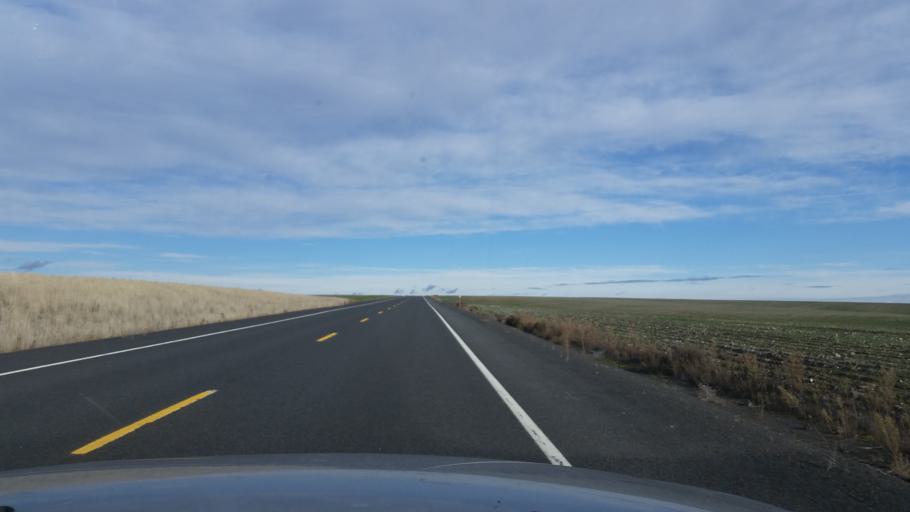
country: US
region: Washington
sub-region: Adams County
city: Ritzville
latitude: 47.3781
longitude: -118.4353
